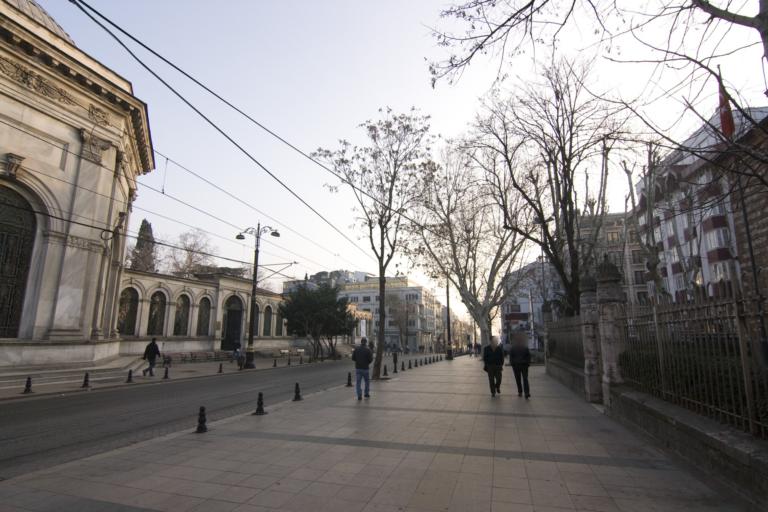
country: TR
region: Istanbul
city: Eminoenue
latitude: 41.0083
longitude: 28.9725
